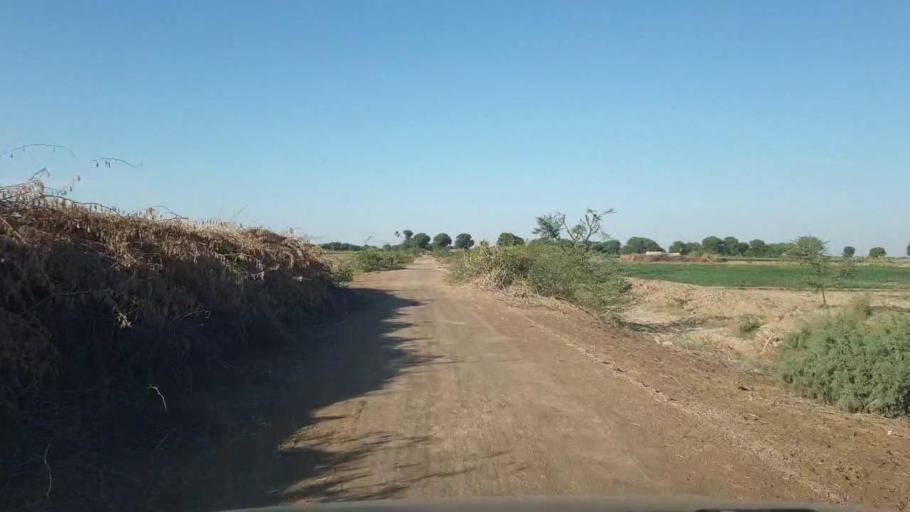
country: PK
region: Sindh
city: Dhoro Naro
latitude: 25.4313
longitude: 69.5438
